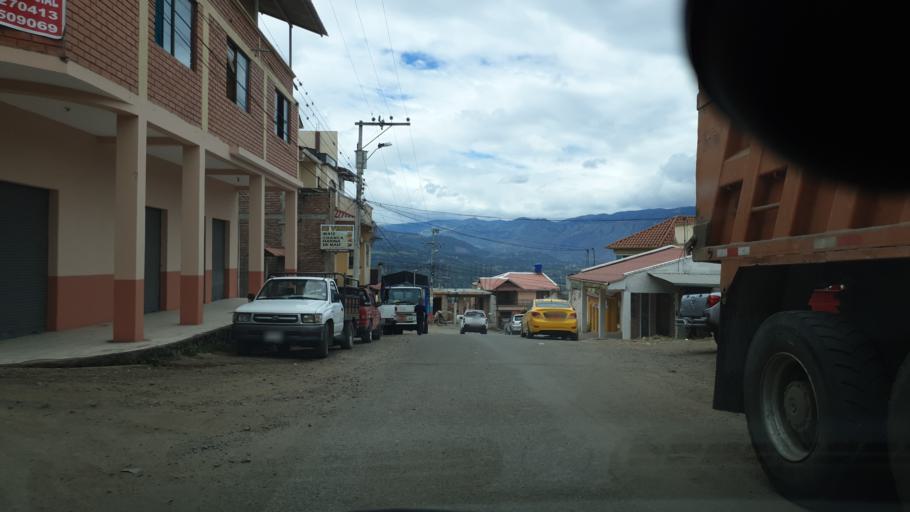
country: EC
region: Azuay
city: Cuenca
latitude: -3.2754
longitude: -79.3131
